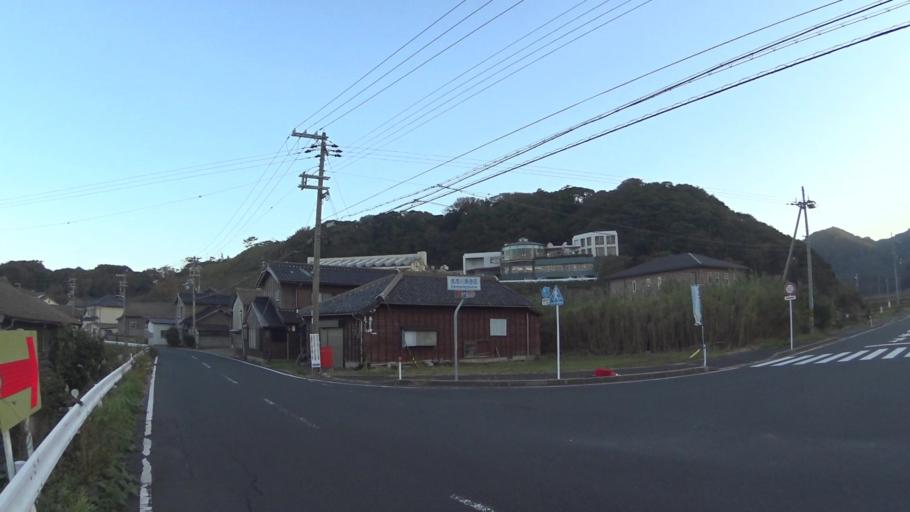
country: JP
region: Kyoto
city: Miyazu
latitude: 35.6907
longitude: 135.0138
